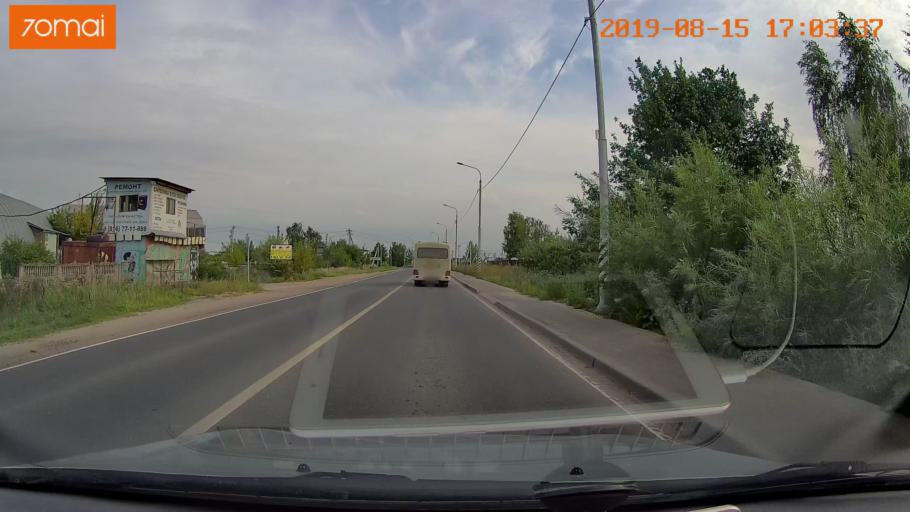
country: RU
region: Moskovskaya
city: Beloozerskiy
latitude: 55.4813
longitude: 38.4016
